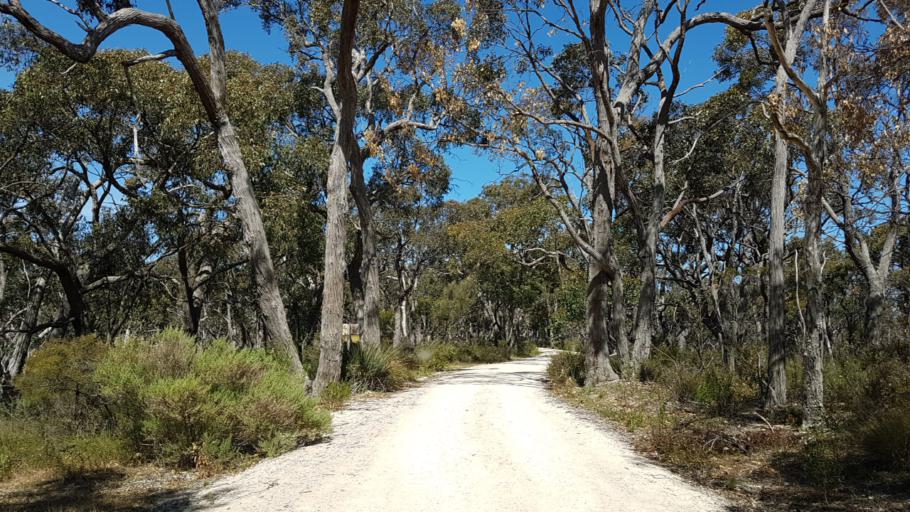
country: AU
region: South Australia
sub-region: Adelaide Hills
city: Adelaide Hills
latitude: -34.9011
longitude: 138.7261
